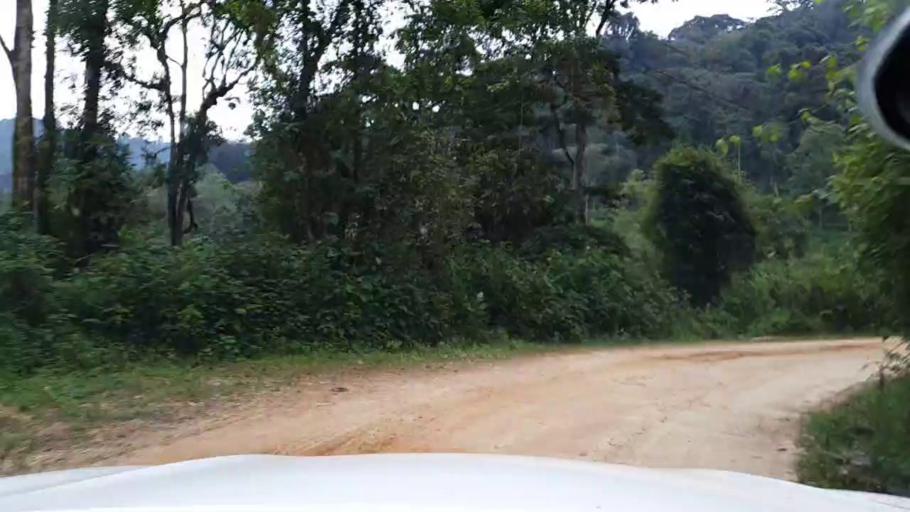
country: RW
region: Western Province
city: Cyangugu
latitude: -2.5663
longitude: 29.2313
